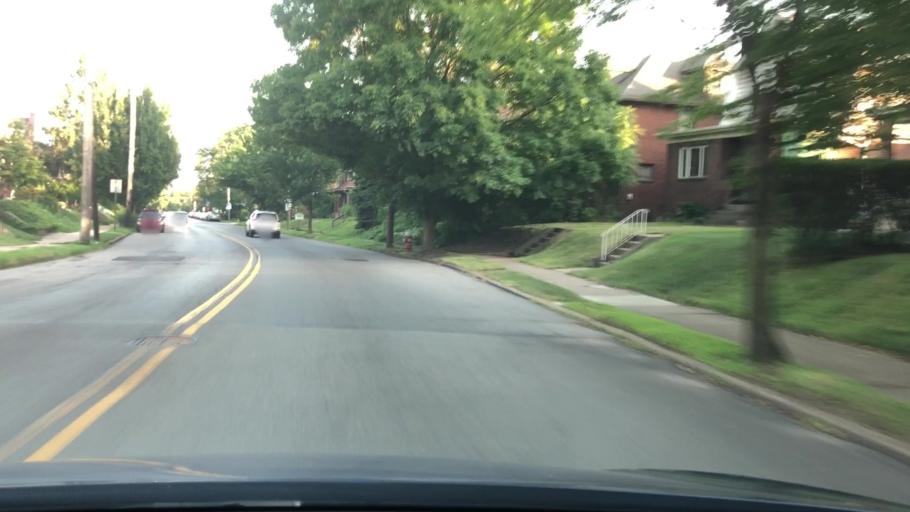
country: US
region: Pennsylvania
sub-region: Allegheny County
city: Edgewood
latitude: 40.4352
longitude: -79.8957
